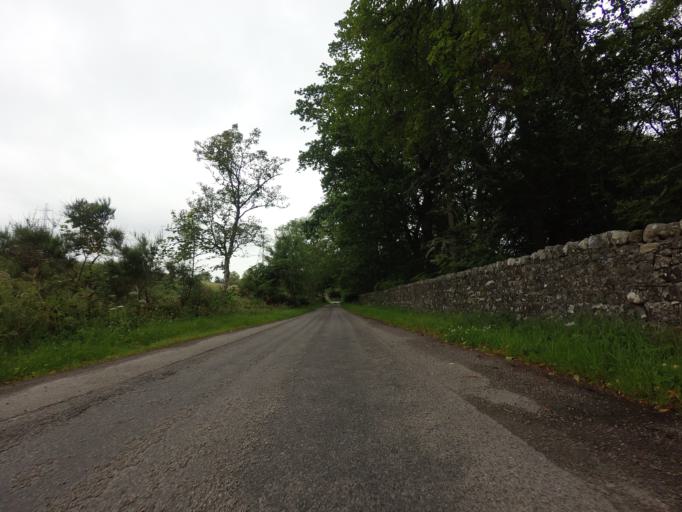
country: GB
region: Scotland
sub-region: Highland
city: Alness
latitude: 57.8914
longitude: -4.3768
